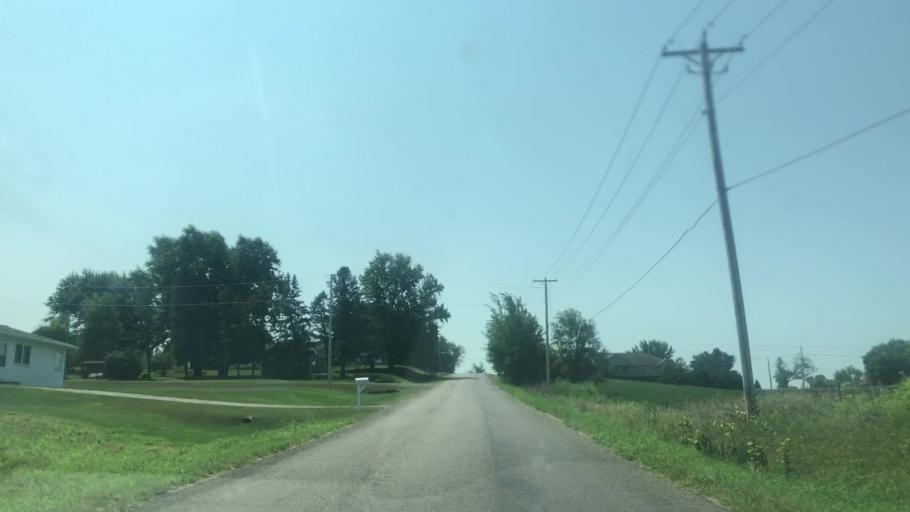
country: US
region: Iowa
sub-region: Marshall County
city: Marshalltown
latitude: 42.0515
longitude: -92.9565
